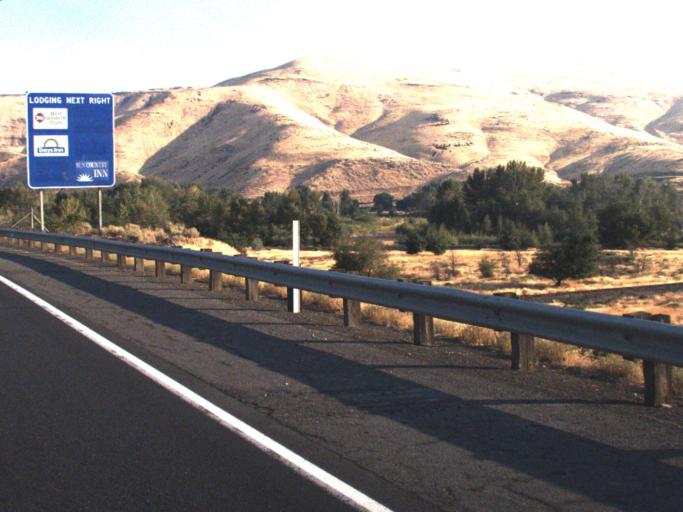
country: US
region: Washington
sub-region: Yakima County
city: Yakima
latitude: 46.6143
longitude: -120.4914
